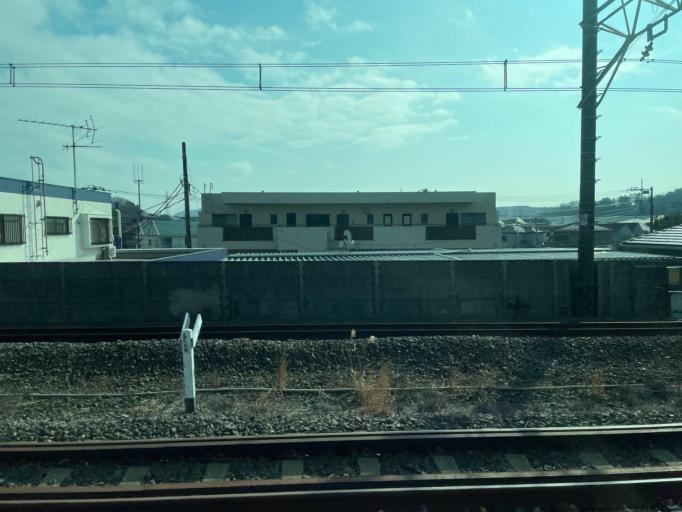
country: JP
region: Kanagawa
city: Kamakura
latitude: 35.3689
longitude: 139.5351
